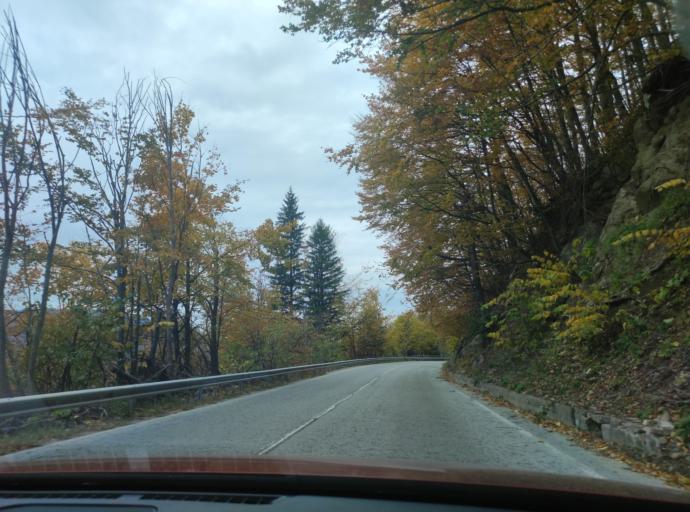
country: BG
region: Montana
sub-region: Obshtina Berkovitsa
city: Berkovitsa
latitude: 43.1462
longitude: 23.1443
